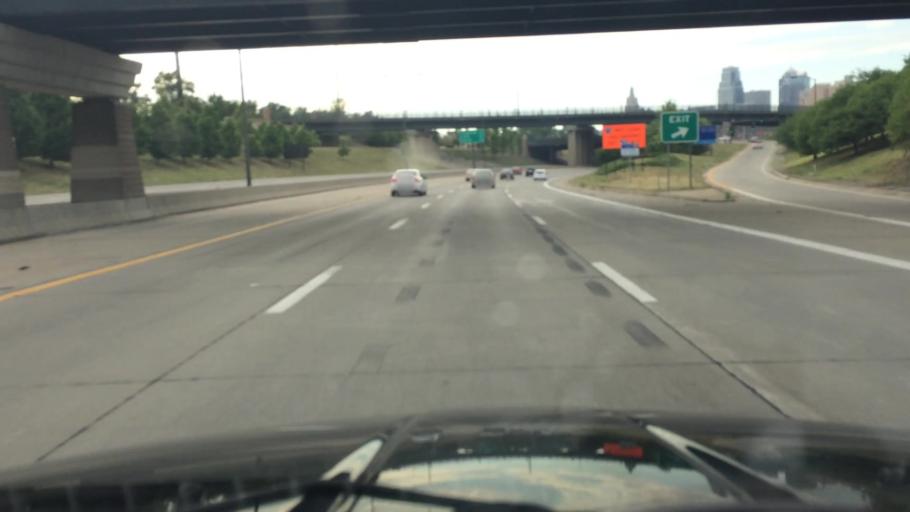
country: US
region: Missouri
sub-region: Jackson County
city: Kansas City
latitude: 39.0843
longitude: -94.5681
